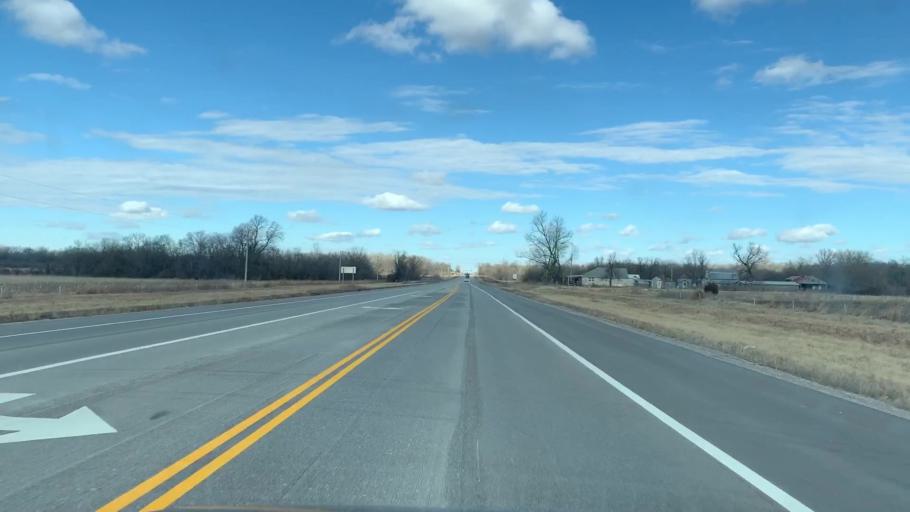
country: US
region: Kansas
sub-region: Cherokee County
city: Columbus
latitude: 37.3117
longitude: -94.8322
